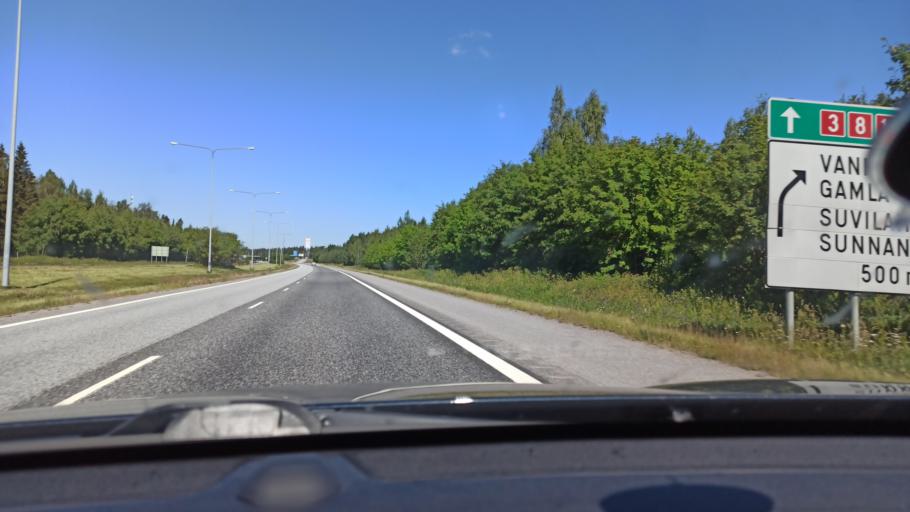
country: FI
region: Ostrobothnia
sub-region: Vaasa
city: Ristinummi
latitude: 63.0633
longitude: 21.7070
